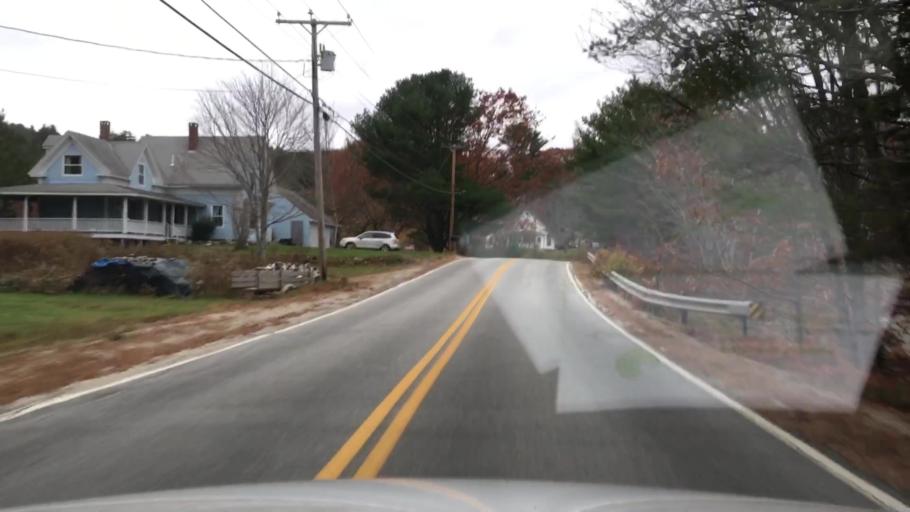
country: US
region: Maine
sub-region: Hancock County
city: Sedgwick
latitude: 44.3785
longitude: -68.5650
